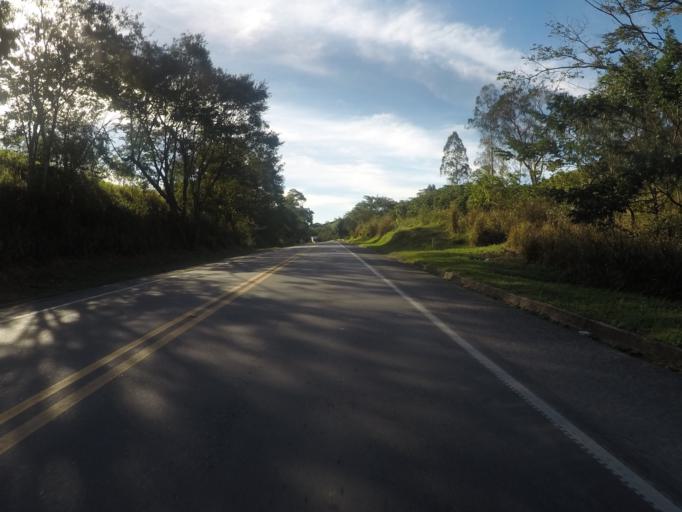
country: BR
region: Espirito Santo
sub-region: Fundao
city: Fundao
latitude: -19.8957
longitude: -40.4117
